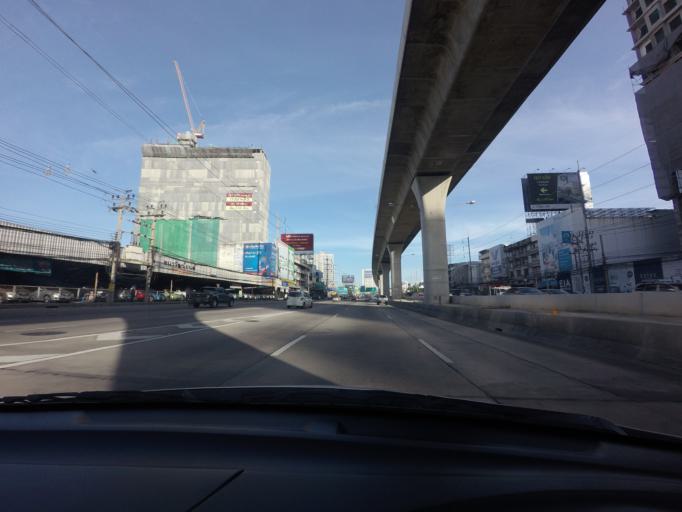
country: TH
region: Nonthaburi
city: Mueang Nonthaburi
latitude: 13.8627
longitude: 100.5011
